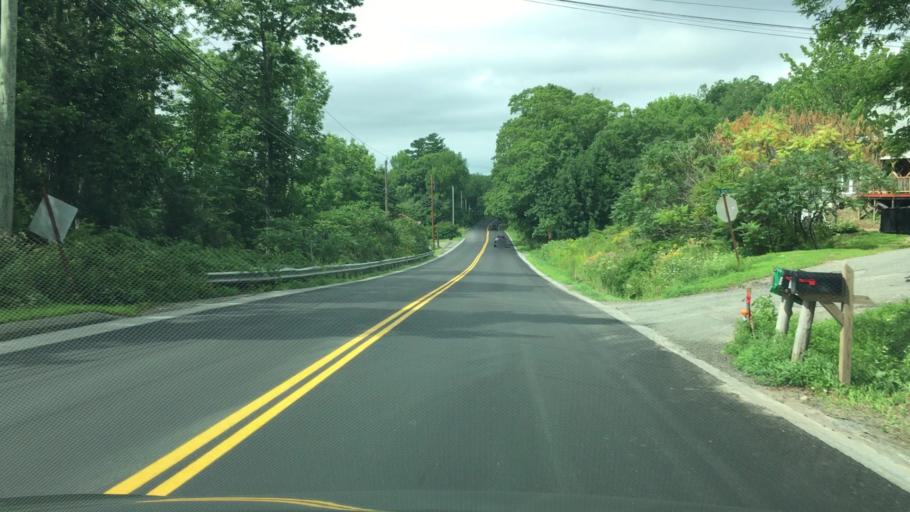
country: US
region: Maine
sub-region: Waldo County
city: Winterport
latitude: 44.6094
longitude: -68.8216
